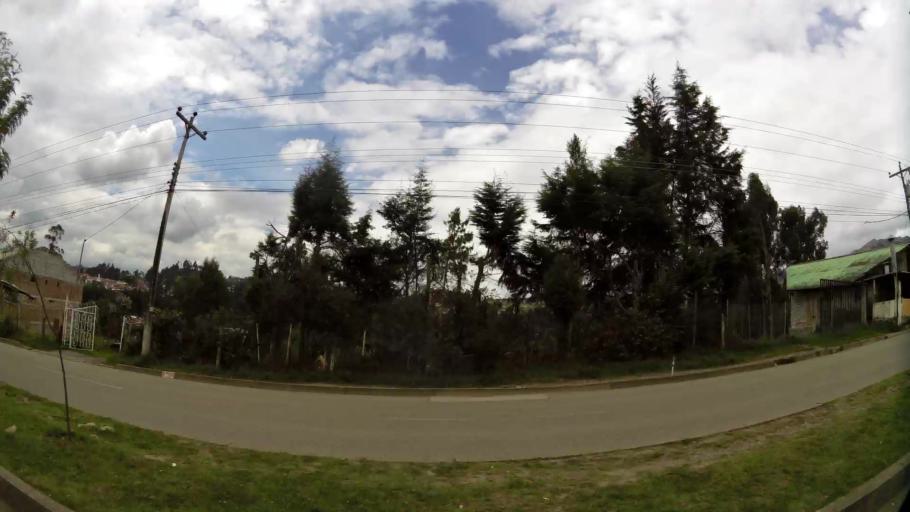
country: EC
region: Azuay
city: Cuenca
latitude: -2.8977
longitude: -79.0532
